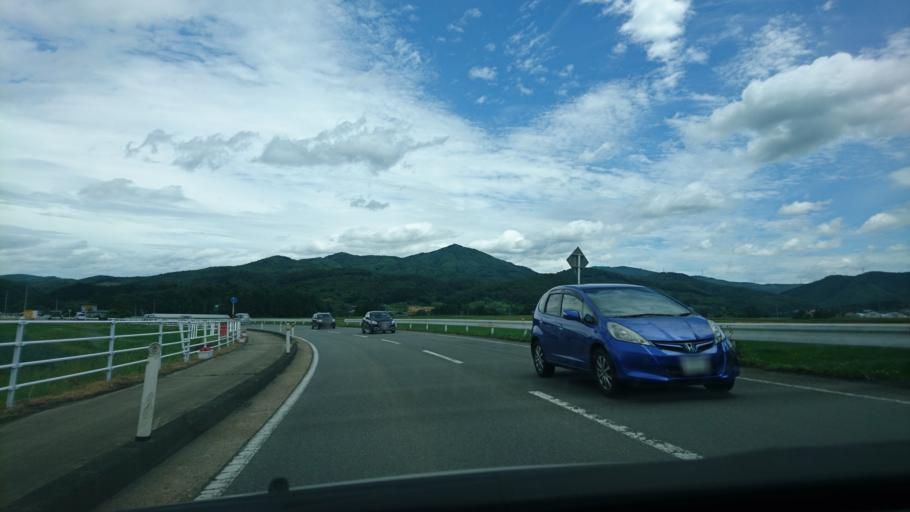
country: JP
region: Iwate
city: Morioka-shi
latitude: 39.6022
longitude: 141.2048
